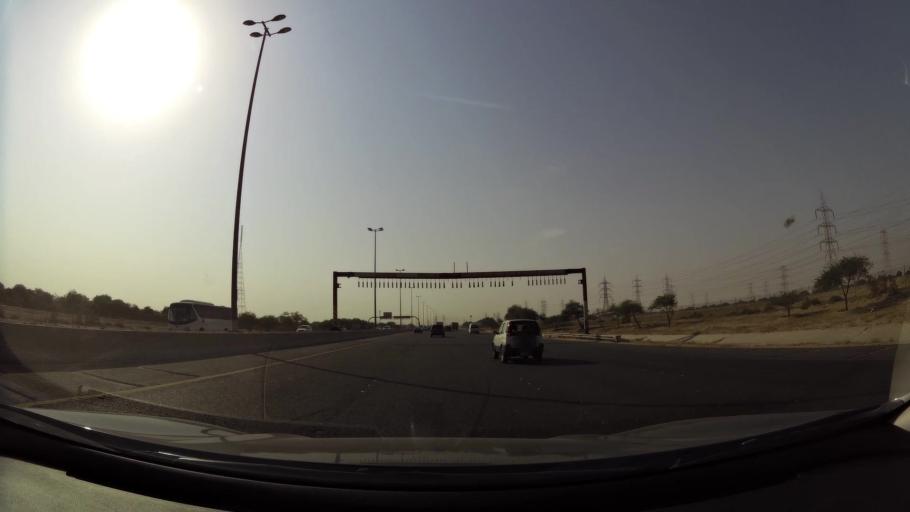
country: KW
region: Al Ahmadi
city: Al Ahmadi
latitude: 29.0868
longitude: 48.0991
